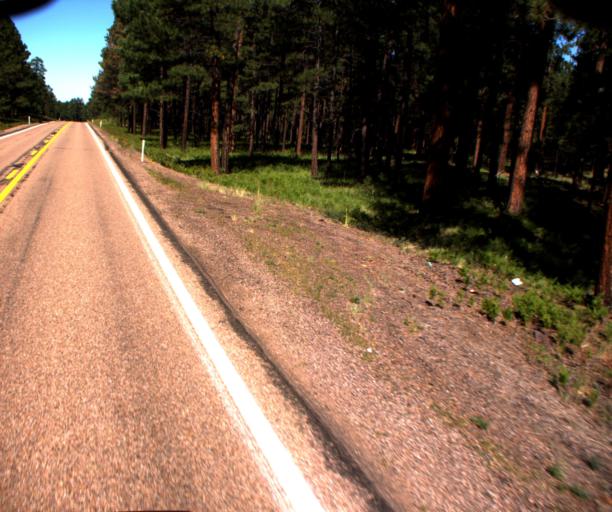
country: US
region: Arizona
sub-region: Navajo County
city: Pinetop-Lakeside
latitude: 34.0527
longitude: -109.7431
